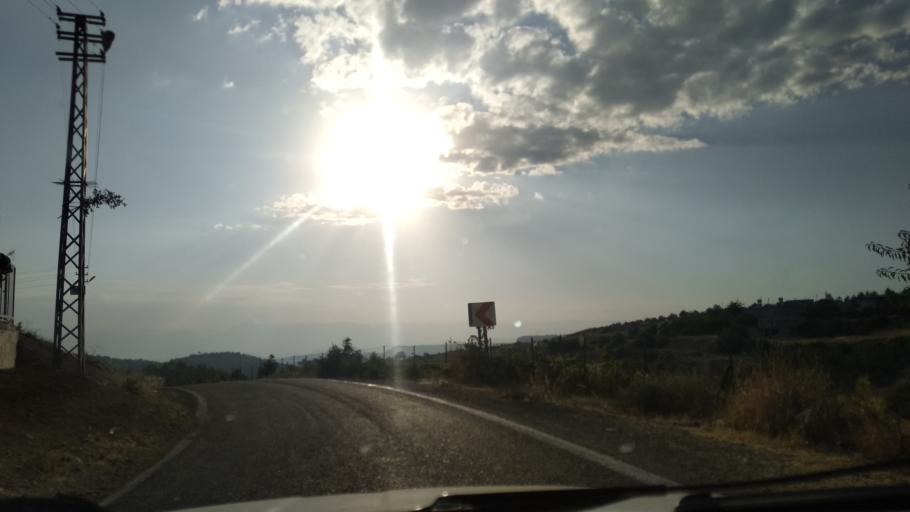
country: TR
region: Mersin
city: Sarikavak
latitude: 36.5772
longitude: 33.6426
